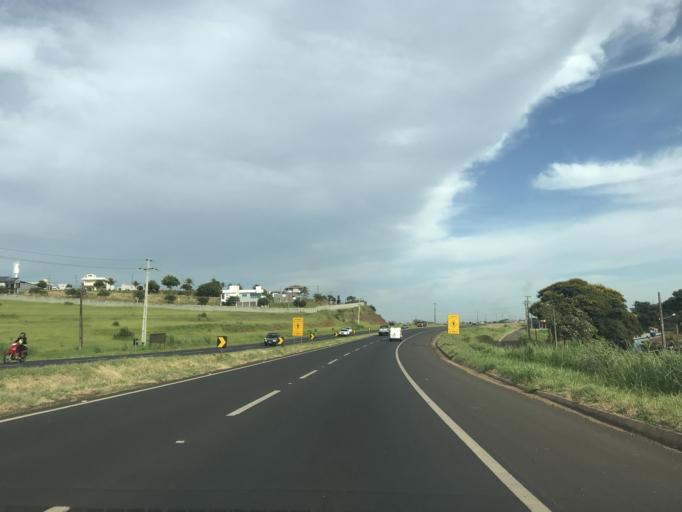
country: BR
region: Parana
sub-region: Mandaguacu
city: Mandaguacu
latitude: -23.3646
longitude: -52.0833
